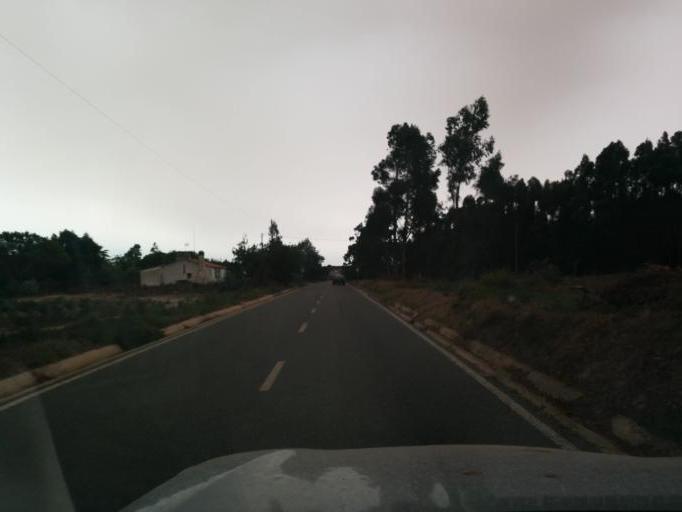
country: PT
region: Beja
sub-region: Odemira
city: Sao Teotonio
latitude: 37.5438
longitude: -8.7478
